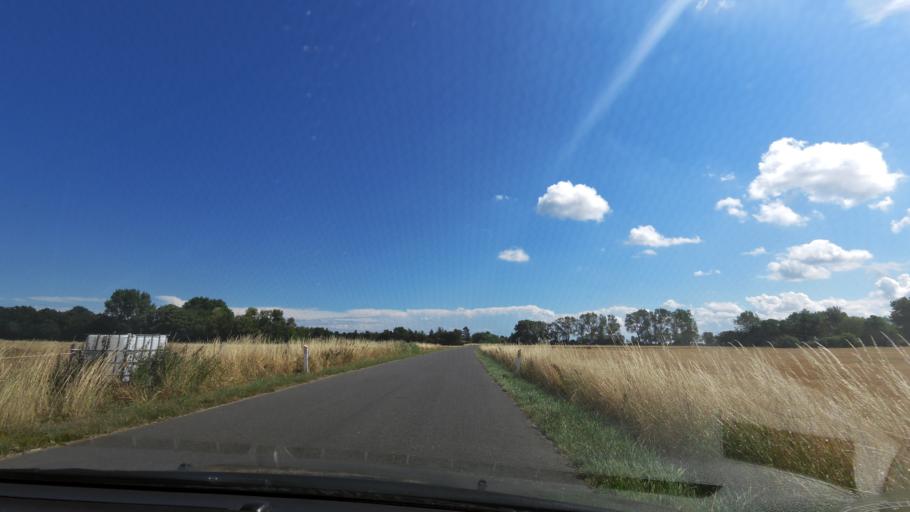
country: DK
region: South Denmark
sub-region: Nordfyns Kommune
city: Otterup
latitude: 55.5516
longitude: 10.4795
